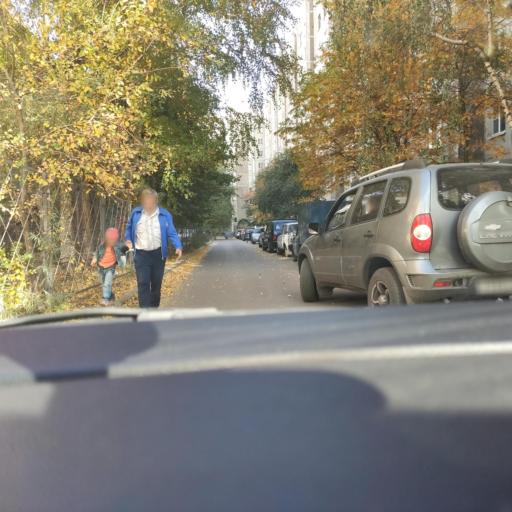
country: RU
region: Voronezj
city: Podgornoye
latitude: 51.7105
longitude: 39.1660
